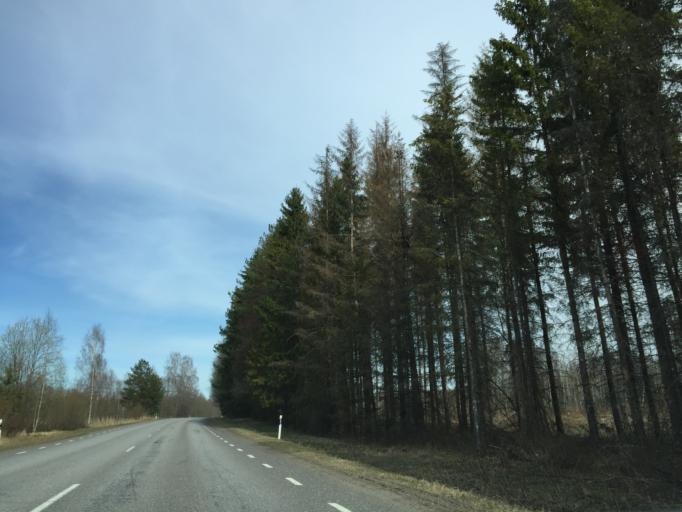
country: EE
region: Vorumaa
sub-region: Antsla vald
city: Vana-Antsla
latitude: 57.9312
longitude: 26.3475
